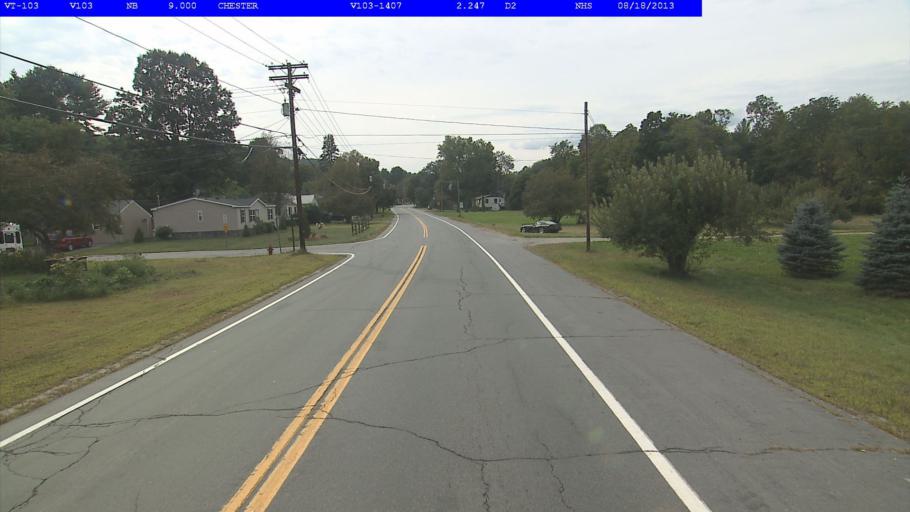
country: US
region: Vermont
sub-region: Windsor County
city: Chester
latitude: 43.2571
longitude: -72.5839
